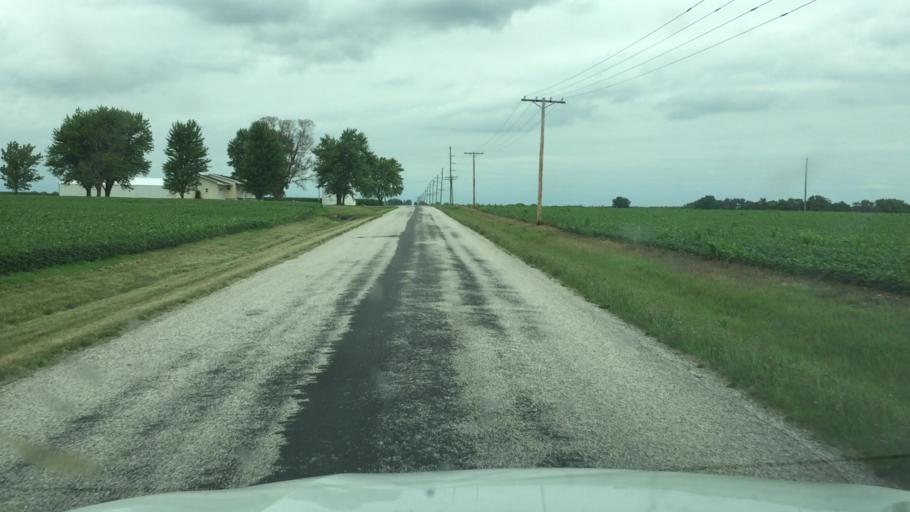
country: US
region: Illinois
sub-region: Hancock County
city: Carthage
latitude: 40.3073
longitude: -91.0830
